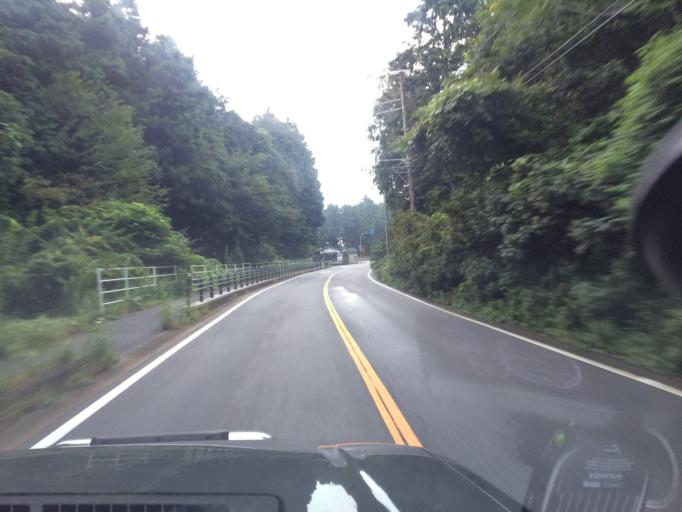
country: JP
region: Hyogo
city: Nishiwaki
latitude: 35.1312
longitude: 135.0128
